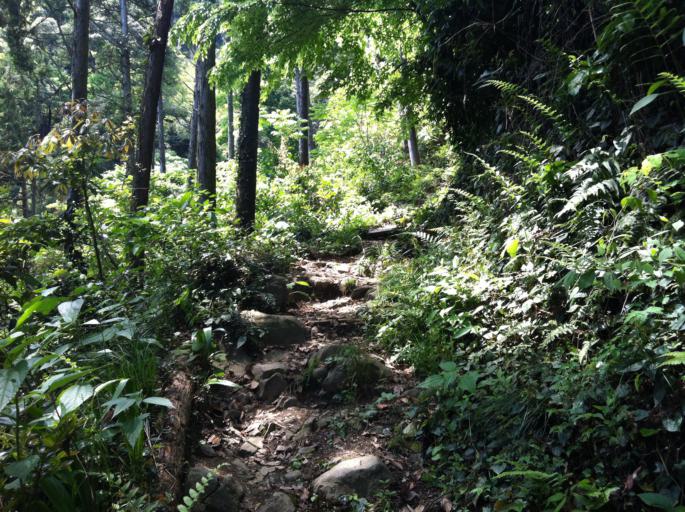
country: JP
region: Shizuoka
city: Shizuoka-shi
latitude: 35.0295
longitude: 138.4358
